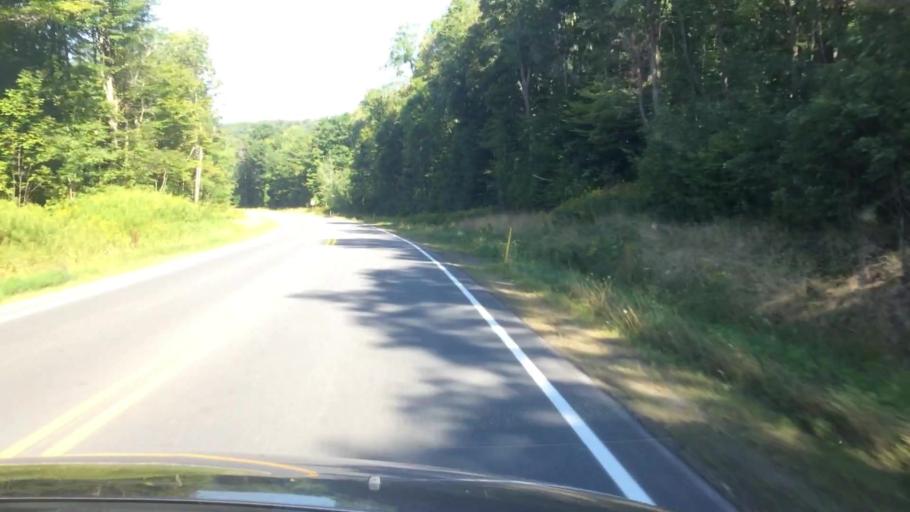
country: US
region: Pennsylvania
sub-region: McKean County
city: Bradford
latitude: 41.8824
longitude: -78.5782
